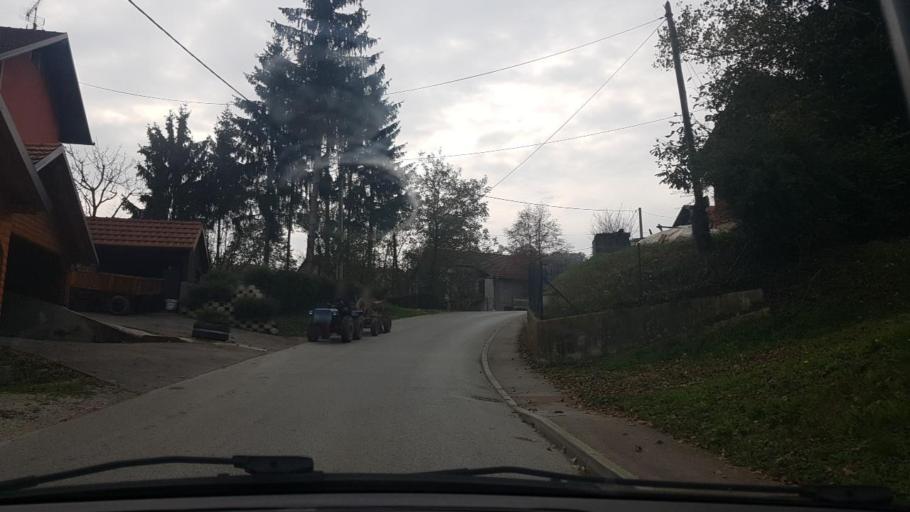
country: SI
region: Rogatec
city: Rogatec
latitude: 46.2103
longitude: 15.7275
